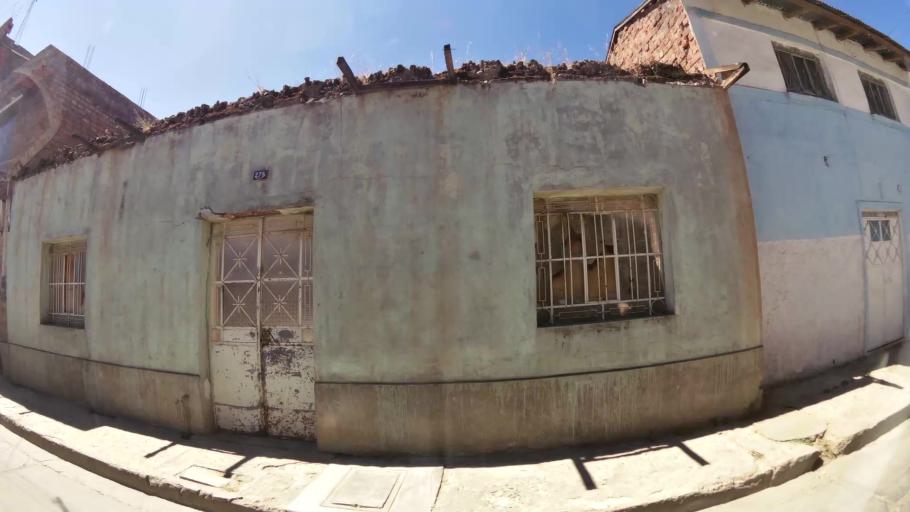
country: PE
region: Junin
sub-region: Provincia de Jauja
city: Jauja
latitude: -11.7701
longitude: -75.5008
